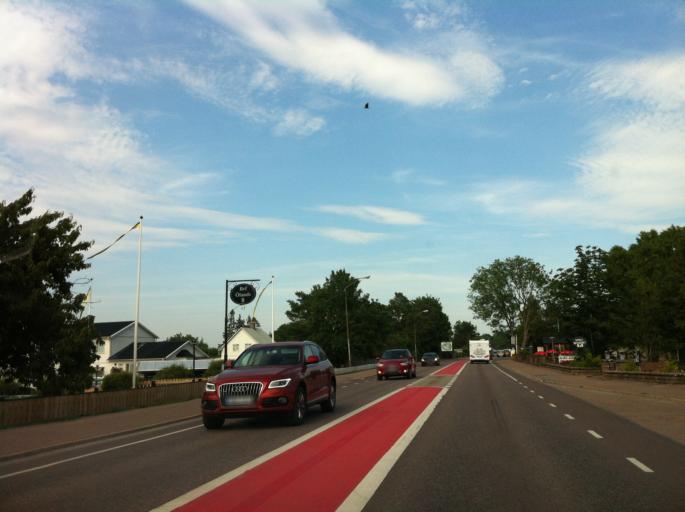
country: SE
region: Kalmar
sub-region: Borgholms Kommun
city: Borgholm
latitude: 56.8782
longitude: 16.7147
